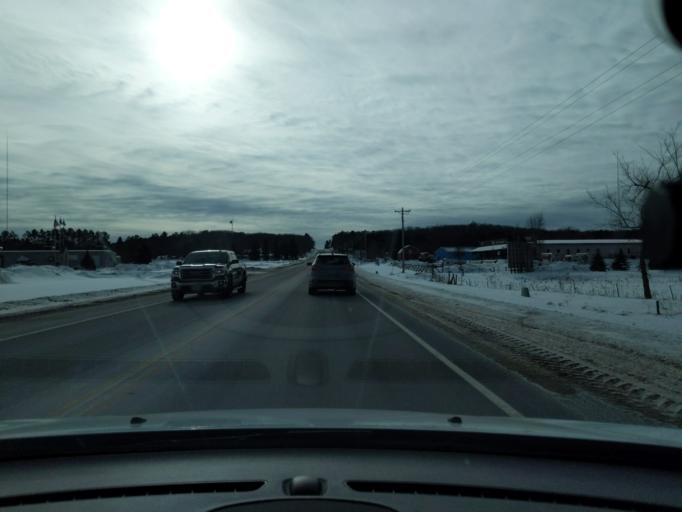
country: US
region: Wisconsin
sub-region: Washburn County
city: Spooner
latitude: 45.8118
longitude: -91.8982
